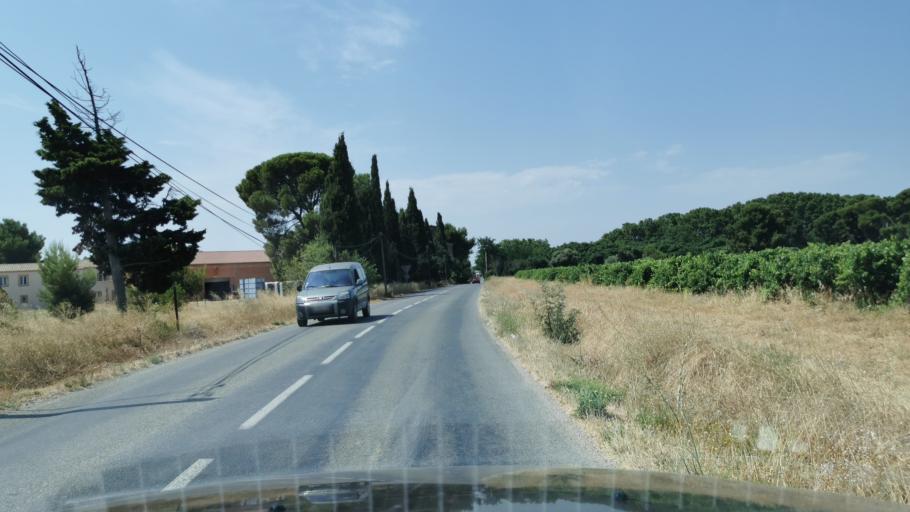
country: FR
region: Languedoc-Roussillon
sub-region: Departement de l'Aude
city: Argeliers
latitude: 43.2864
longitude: 2.9034
